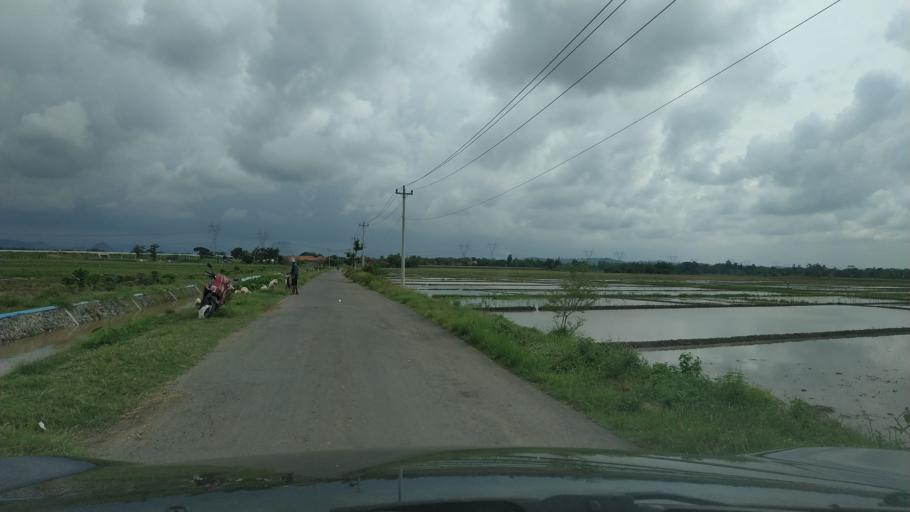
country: ID
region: Central Java
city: Pemalang
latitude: -6.9307
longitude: 109.3385
